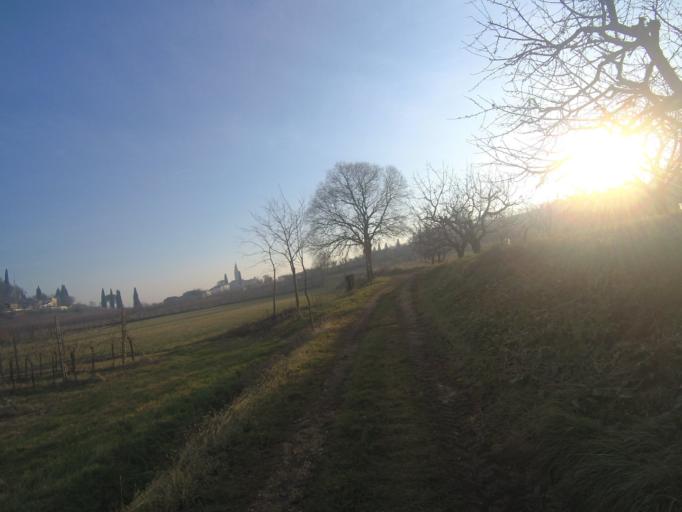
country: IT
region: Veneto
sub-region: Provincia di Vicenza
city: Lumignano
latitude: 45.4477
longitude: 11.5835
